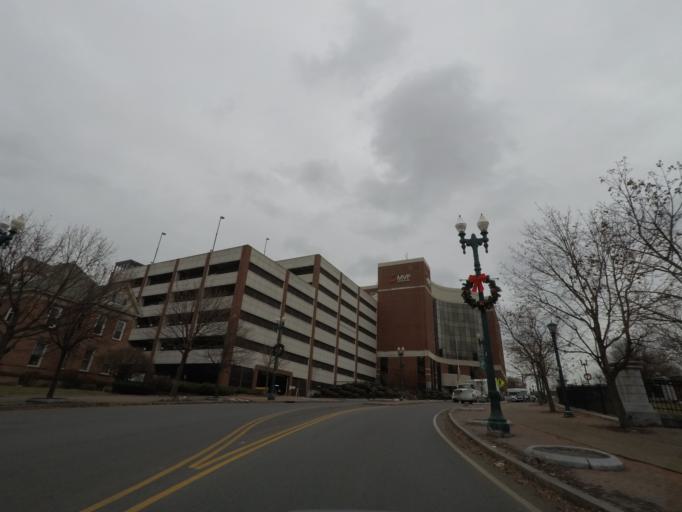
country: US
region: New York
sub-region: Schenectady County
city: Schenectady
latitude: 42.8114
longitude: -73.9393
